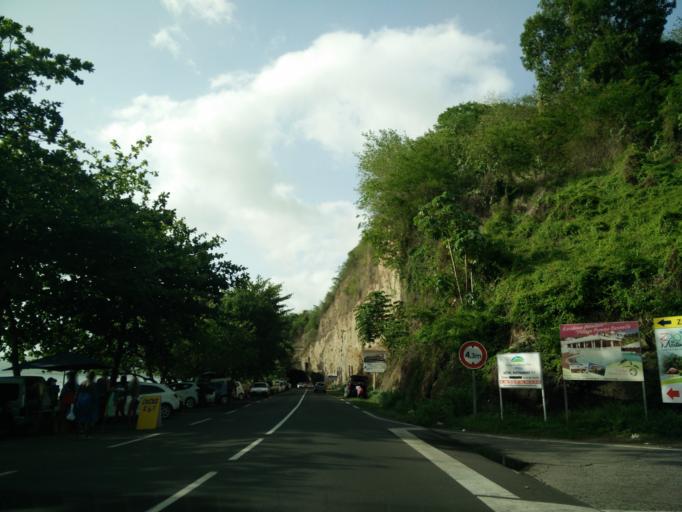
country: MQ
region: Martinique
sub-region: Martinique
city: Saint-Pierre
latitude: 14.7288
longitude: -61.1797
